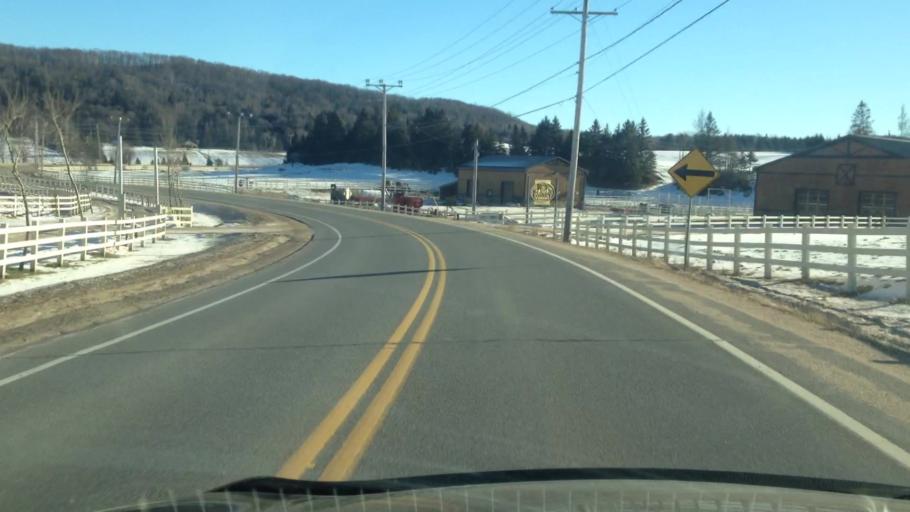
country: CA
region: Quebec
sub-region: Laurentides
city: Mont-Tremblant
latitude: 46.0408
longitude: -74.6057
